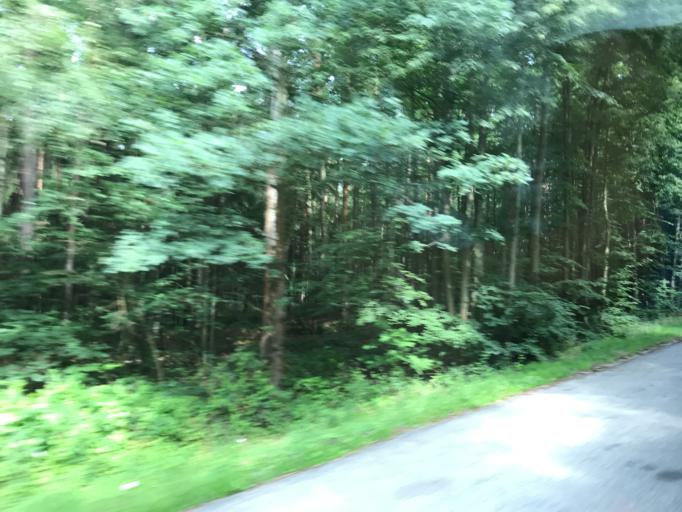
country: CZ
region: Jihocesky
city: Vcelna
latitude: 48.9134
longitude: 14.4511
